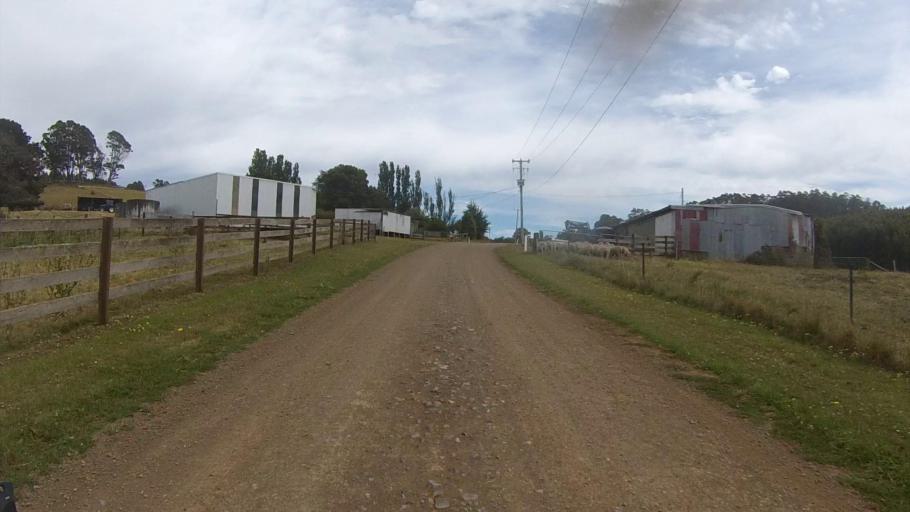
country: AU
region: Tasmania
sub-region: Sorell
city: Sorell
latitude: -42.7265
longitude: 147.7542
